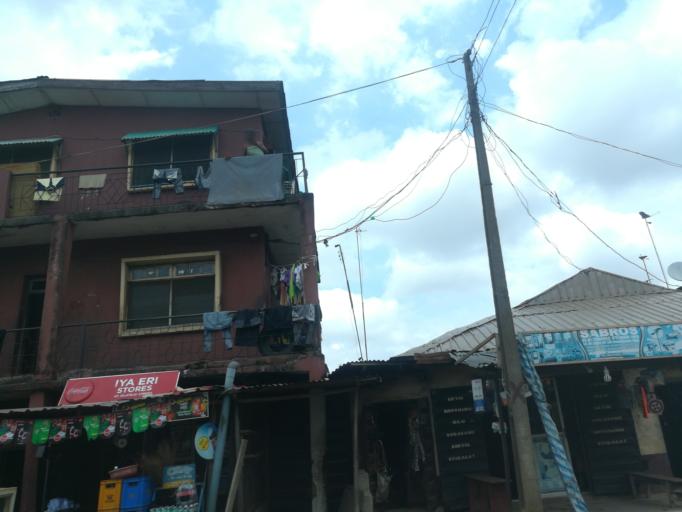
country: NG
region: Lagos
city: Mushin
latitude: 6.5342
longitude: 3.3593
